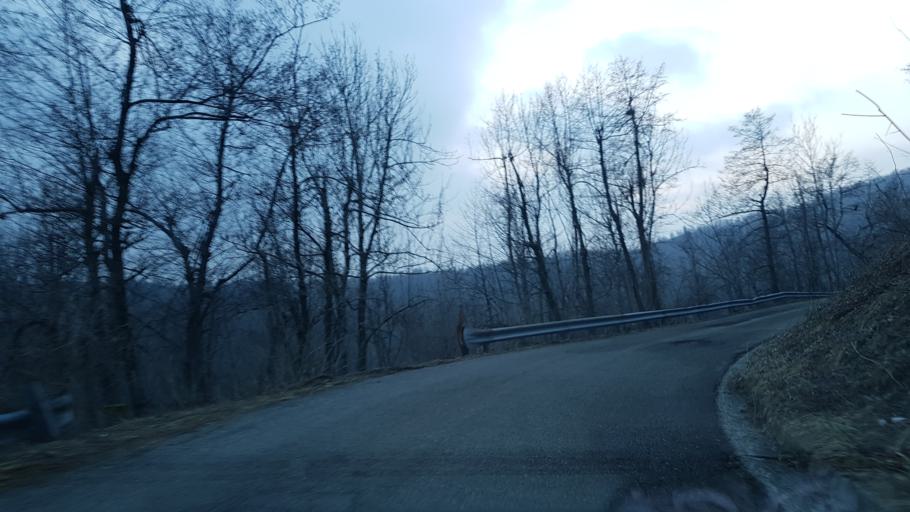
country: IT
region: Friuli Venezia Giulia
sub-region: Provincia di Udine
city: Taipana
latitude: 46.2089
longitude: 13.3682
